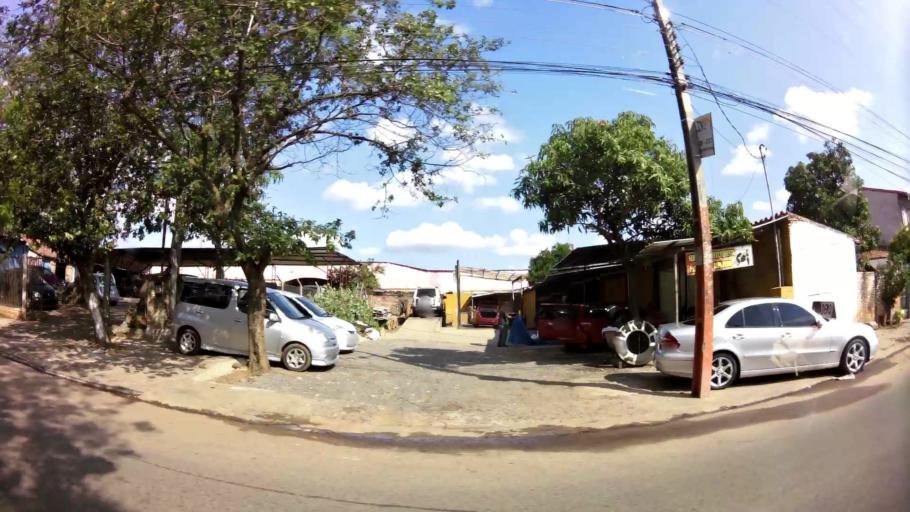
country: PY
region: Central
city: Fernando de la Mora
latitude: -25.3194
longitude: -57.5270
